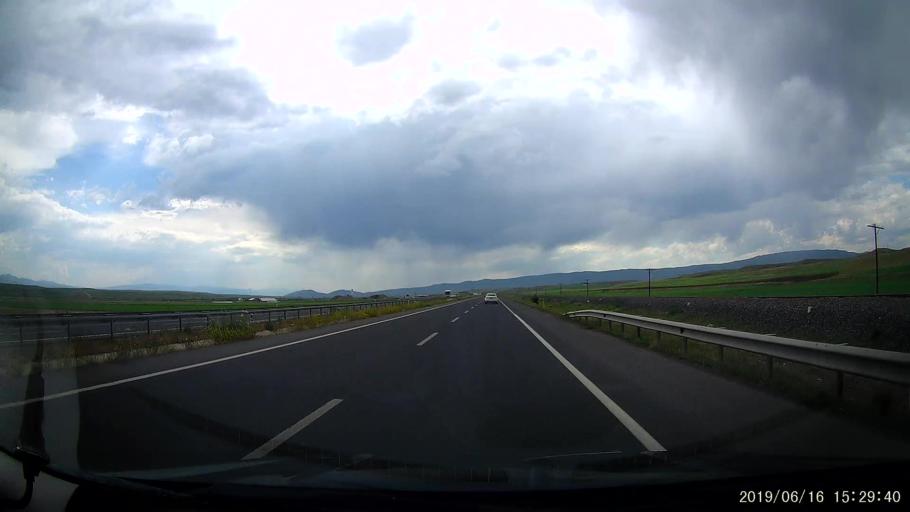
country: TR
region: Erzurum
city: Horasan
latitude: 40.0322
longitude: 42.1263
